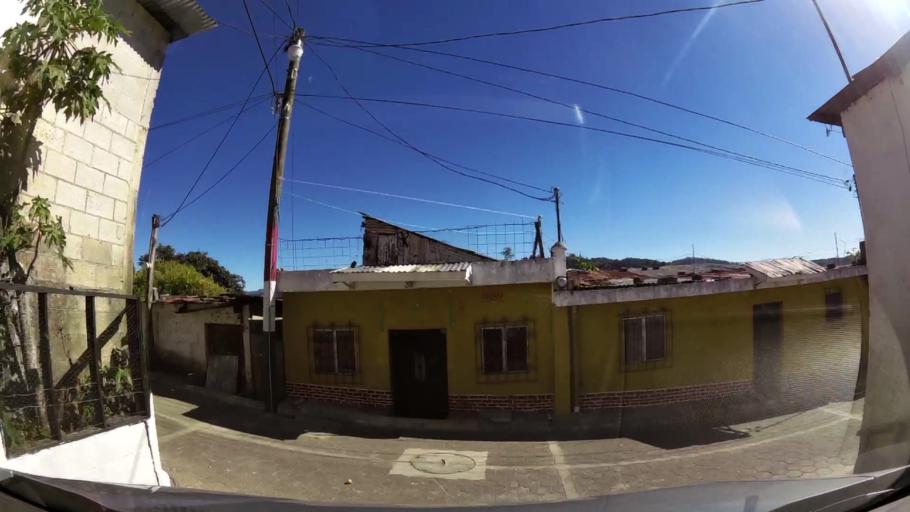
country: GT
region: Guatemala
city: Fraijanes
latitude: 14.4637
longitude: -90.4366
